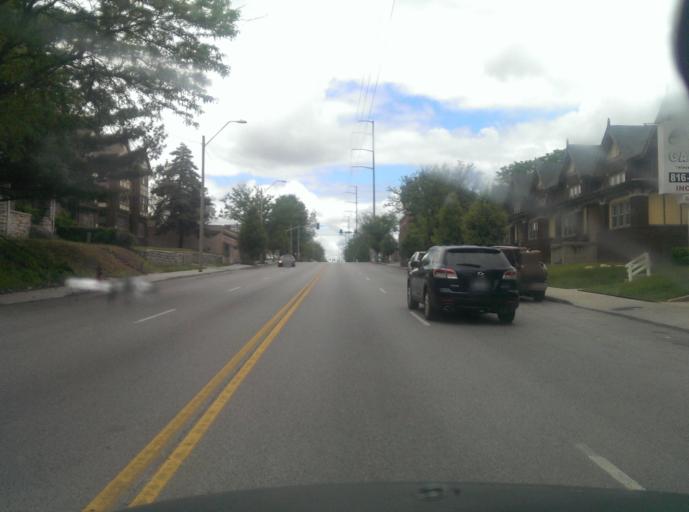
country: US
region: Kansas
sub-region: Johnson County
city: Westwood
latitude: 39.0512
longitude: -94.5724
